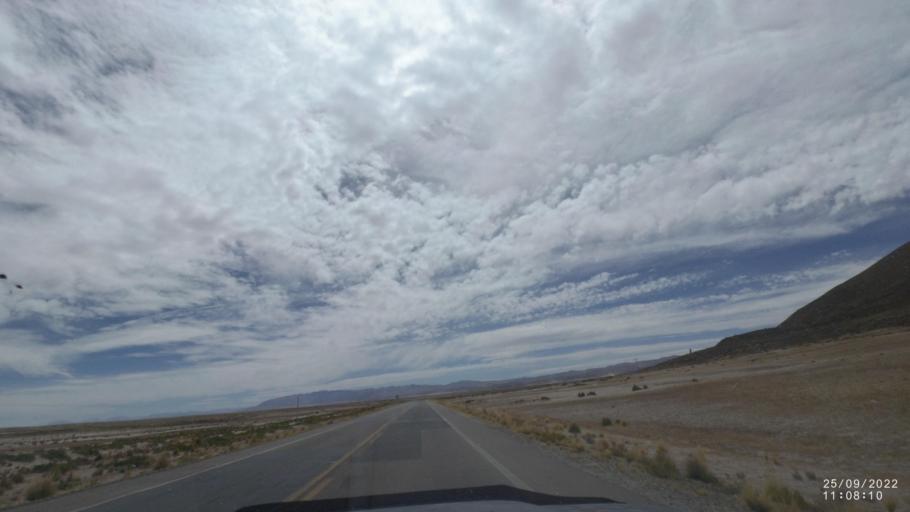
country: BO
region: Oruro
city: Challapata
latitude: -19.3316
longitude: -66.8512
